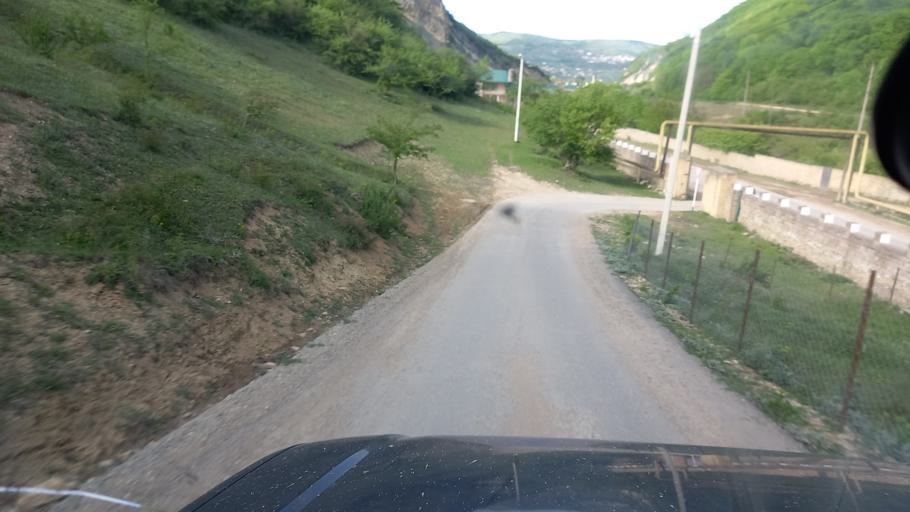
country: RU
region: Dagestan
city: Khuchni
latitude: 41.9650
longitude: 47.9588
